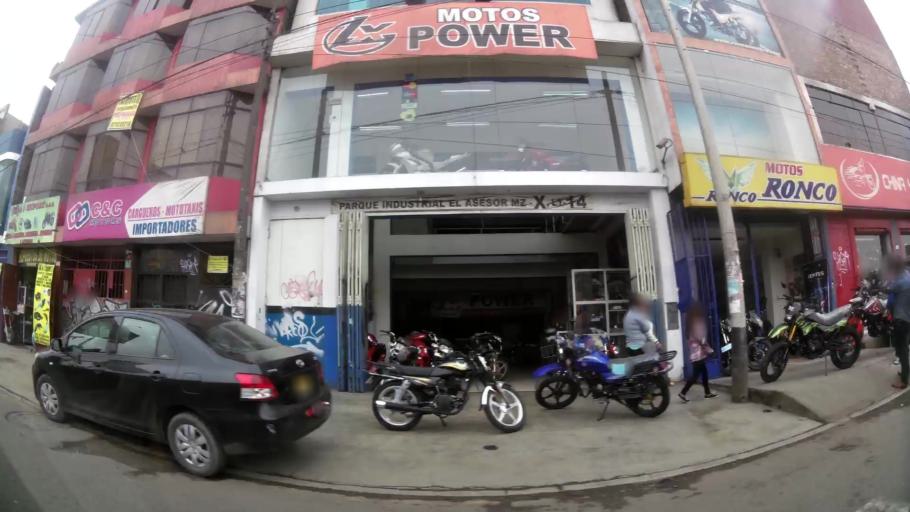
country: PE
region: Lima
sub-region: Lima
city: Vitarte
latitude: -12.0409
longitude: -76.9345
